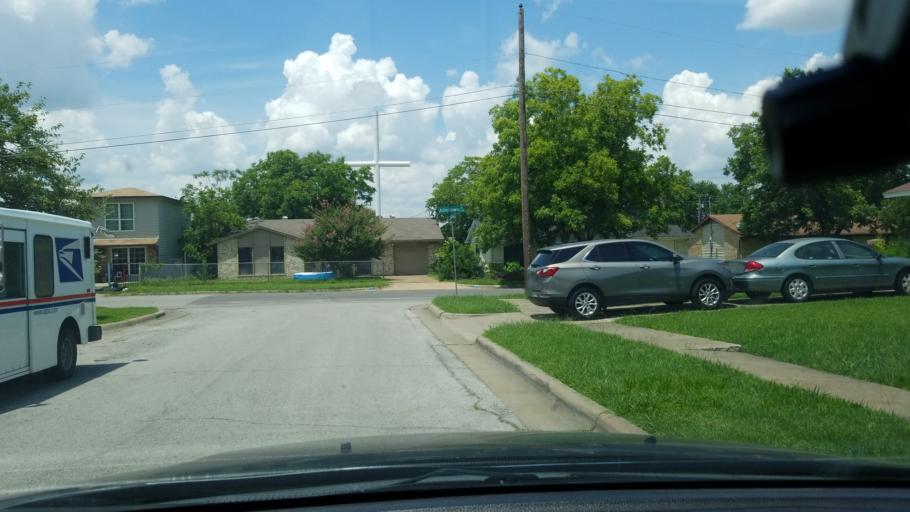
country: US
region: Texas
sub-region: Dallas County
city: Balch Springs
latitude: 32.7416
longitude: -96.6462
